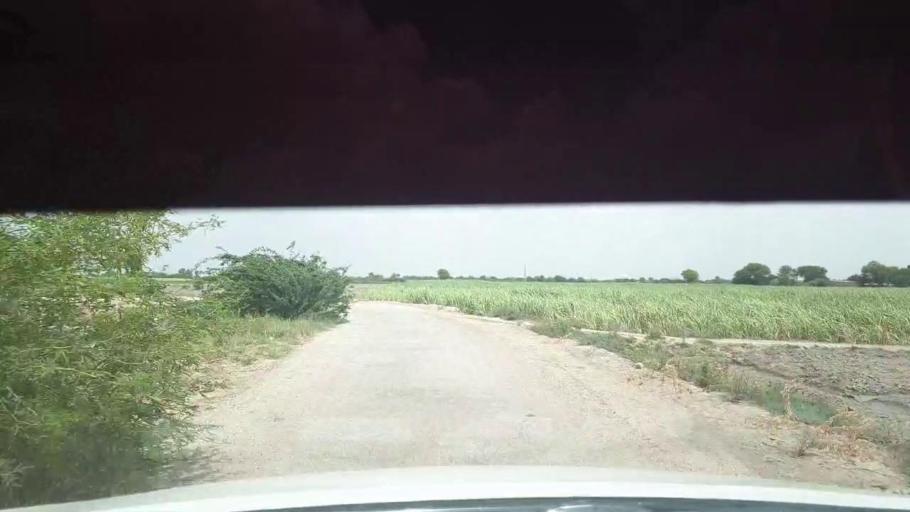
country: PK
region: Sindh
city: Kadhan
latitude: 24.5432
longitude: 69.1250
